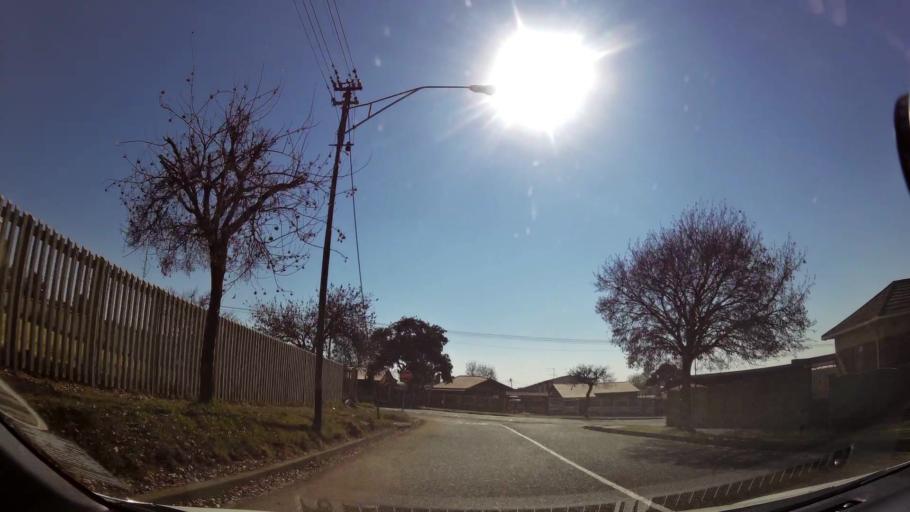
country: ZA
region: Gauteng
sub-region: City of Johannesburg Metropolitan Municipality
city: Johannesburg
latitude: -26.2537
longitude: 28.0898
